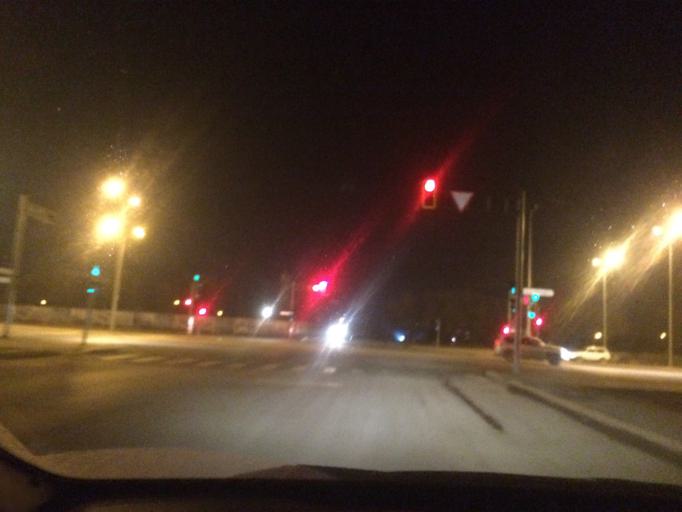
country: KZ
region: Astana Qalasy
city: Astana
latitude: 51.1909
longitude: 71.3338
